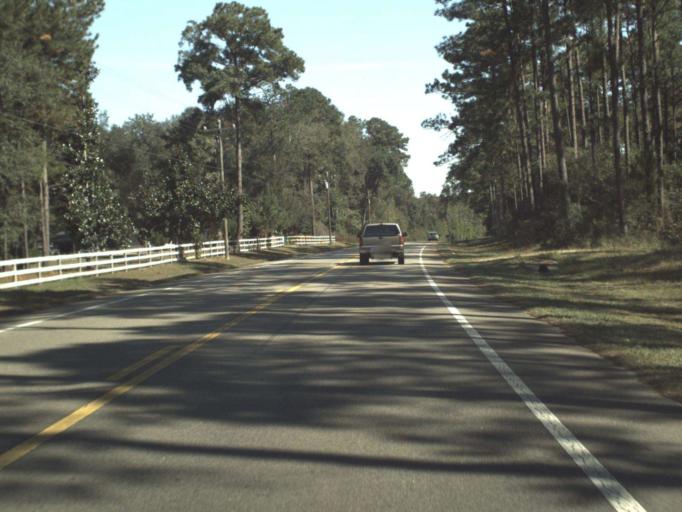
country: US
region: Florida
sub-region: Gadsden County
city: Gretna
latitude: 30.5909
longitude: -84.6858
